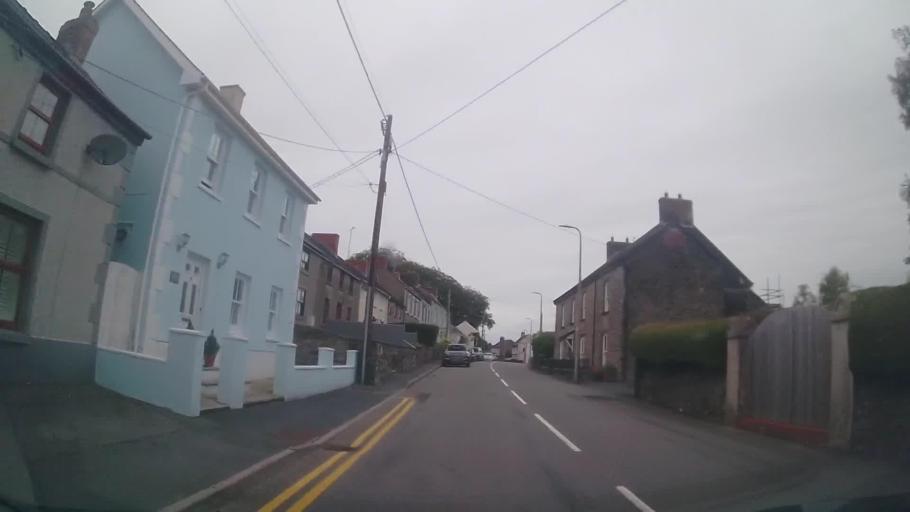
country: GB
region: Wales
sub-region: Carmarthenshire
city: Saint Clears
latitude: 51.8120
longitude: -4.4960
